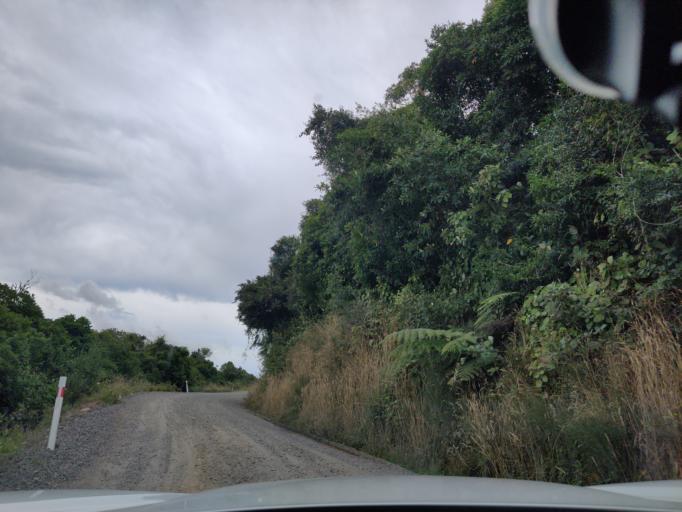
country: NZ
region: Wellington
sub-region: Masterton District
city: Masterton
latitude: -41.0404
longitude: 175.4099
